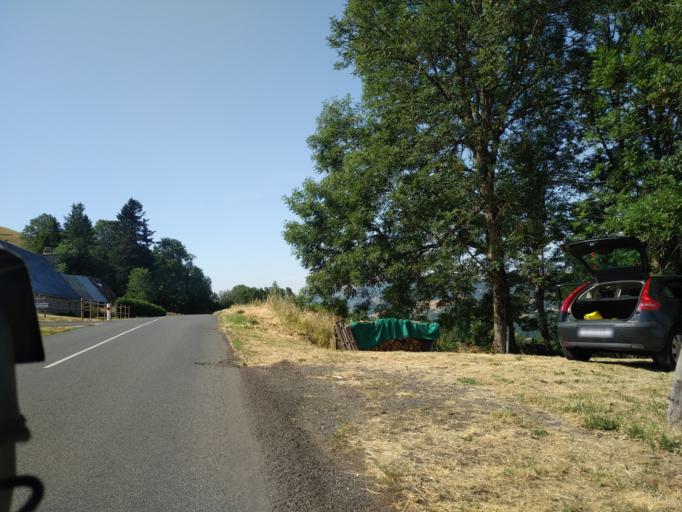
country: FR
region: Auvergne
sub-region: Departement du Cantal
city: Riom-es-Montagnes
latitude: 45.2257
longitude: 2.7259
